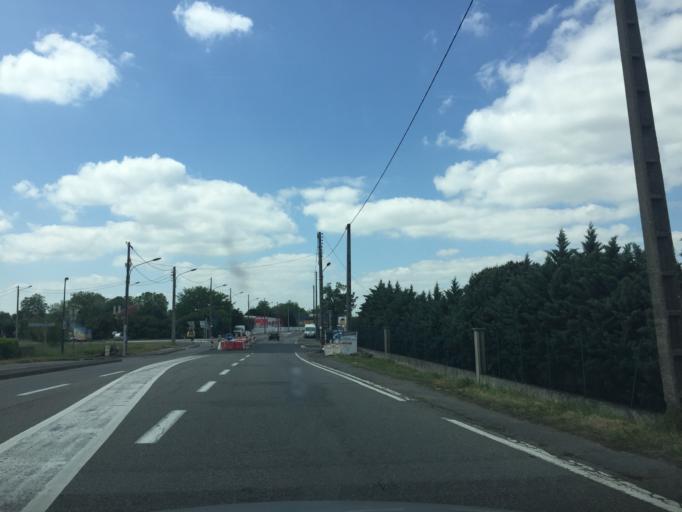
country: FR
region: Midi-Pyrenees
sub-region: Departement de la Haute-Garonne
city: Aucamville
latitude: 43.6499
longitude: 1.4299
